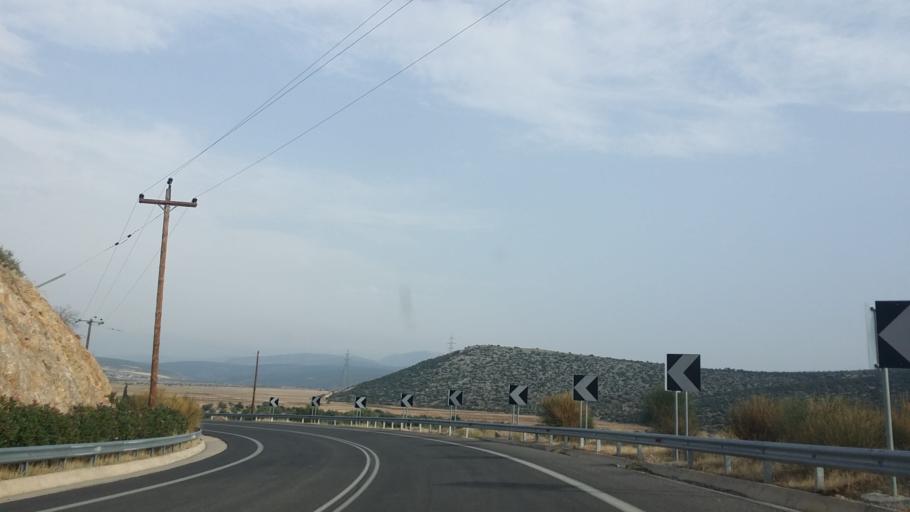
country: GR
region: Central Greece
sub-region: Nomos Voiotias
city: Korini
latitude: 38.2489
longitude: 22.9300
